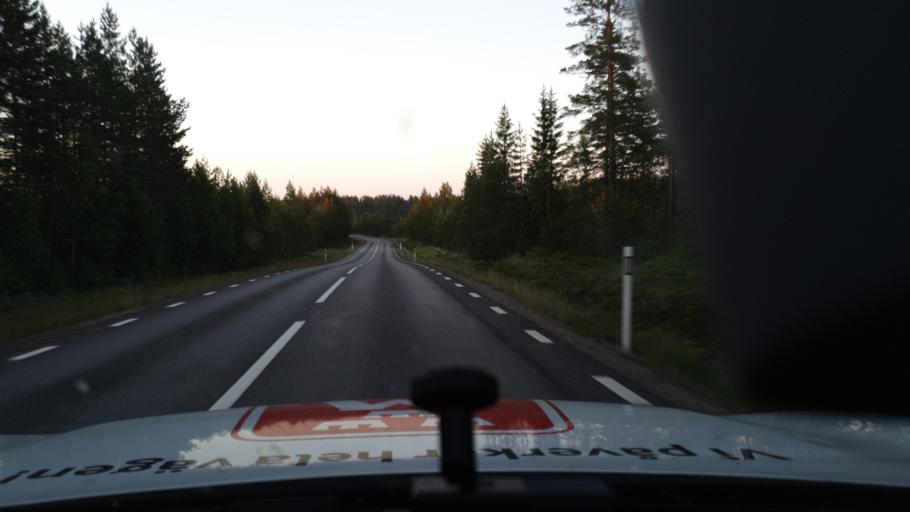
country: SE
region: Vaermland
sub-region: Torsby Kommun
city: Torsby
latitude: 60.3656
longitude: 13.1926
